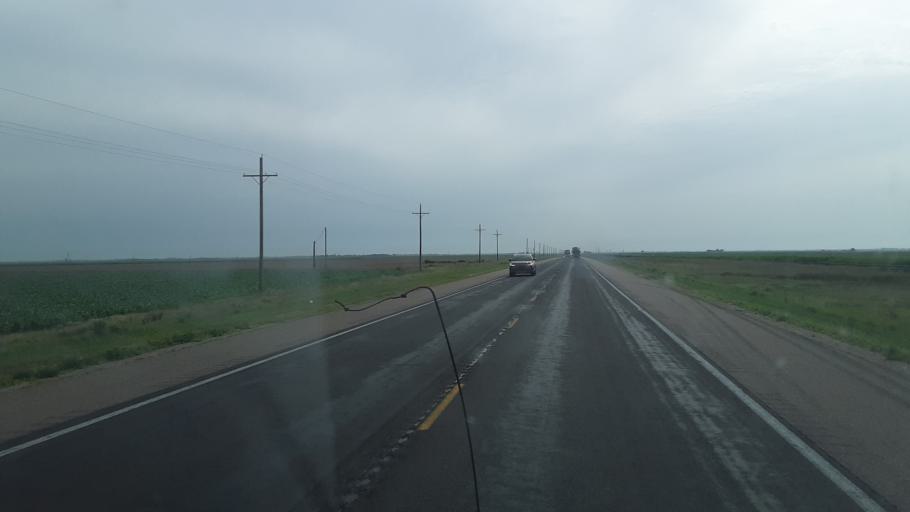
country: US
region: Kansas
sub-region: Edwards County
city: Kinsley
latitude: 37.8938
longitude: -99.5442
